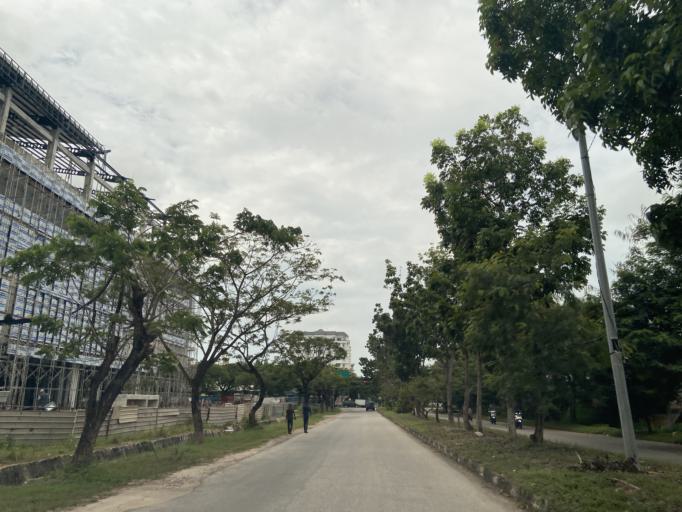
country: SG
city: Singapore
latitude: 1.1290
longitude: 104.0464
